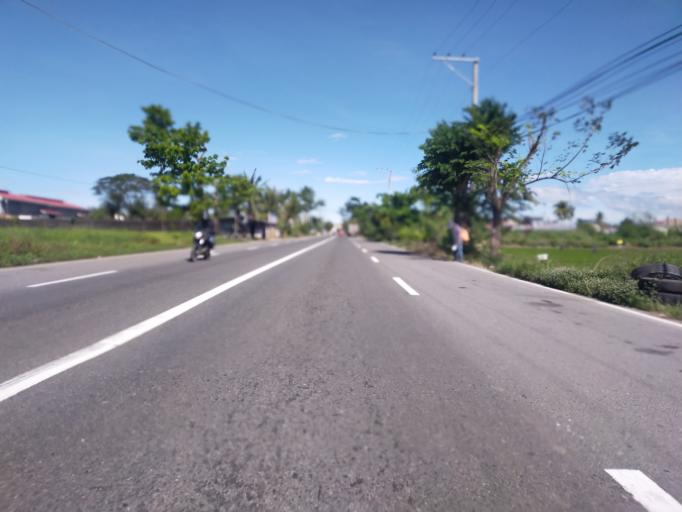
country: PH
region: Central Luzon
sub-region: Province of Bulacan
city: Bulualto
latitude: 15.2347
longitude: 120.9549
